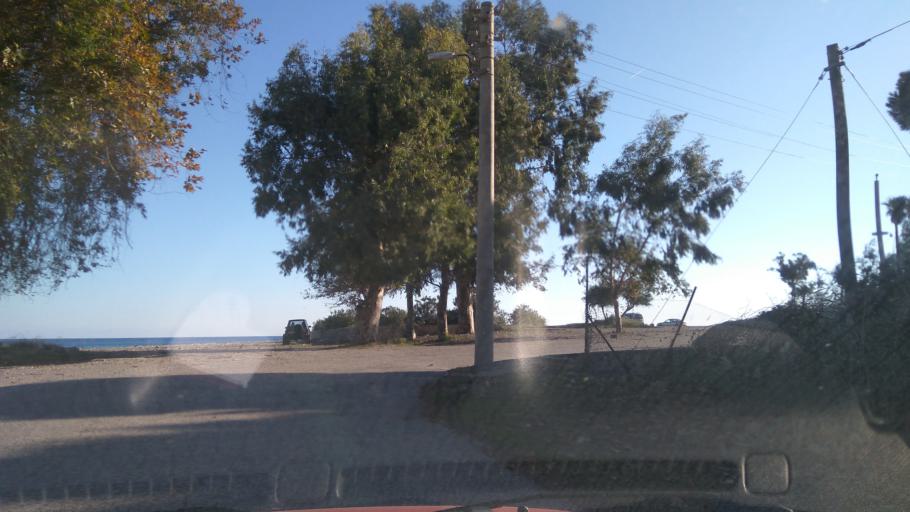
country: TR
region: Antalya
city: Kemer
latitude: 36.5612
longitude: 30.5724
